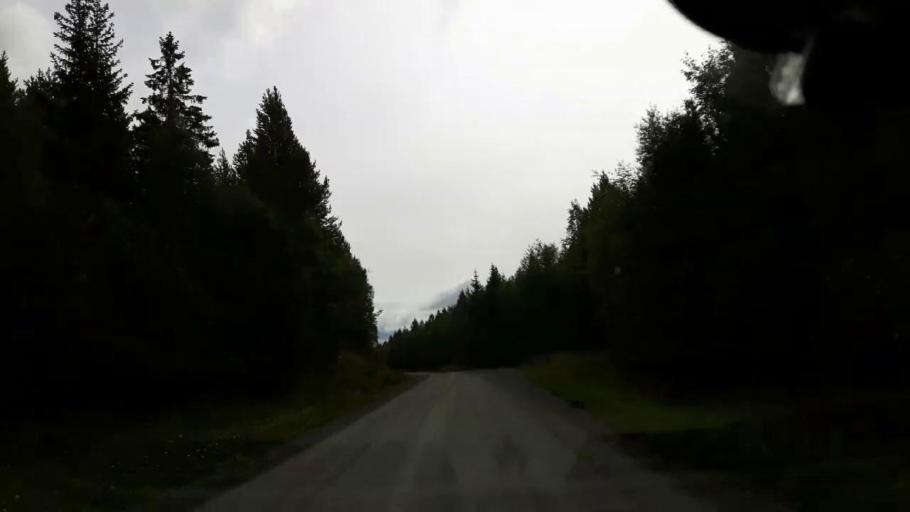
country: SE
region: Jaemtland
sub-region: Krokoms Kommun
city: Valla
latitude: 63.6574
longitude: 13.9760
